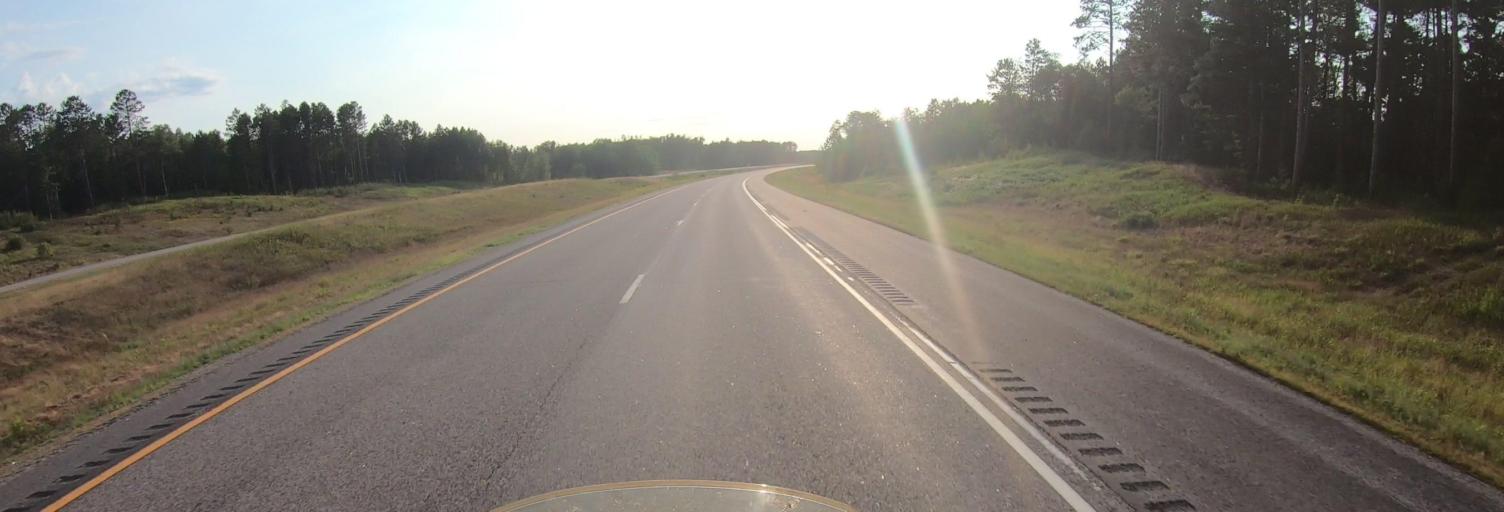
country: US
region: Minnesota
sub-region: Saint Louis County
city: Mountain Iron
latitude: 47.6601
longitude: -92.6090
